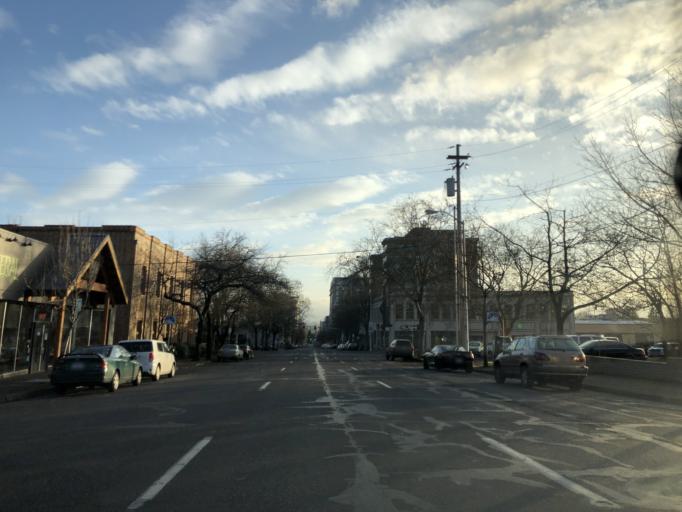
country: US
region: Washington
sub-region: Clark County
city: Vancouver
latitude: 45.6304
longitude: -122.6727
